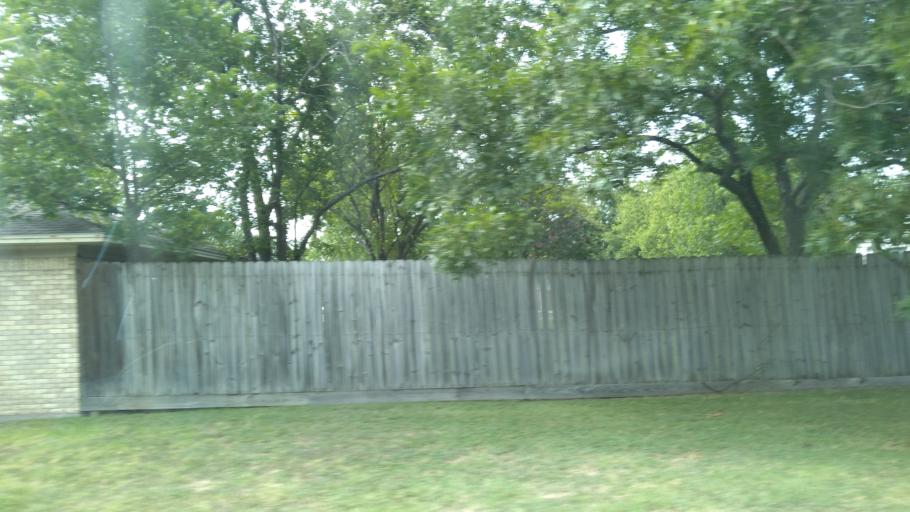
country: US
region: Texas
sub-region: Navarro County
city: Corsicana
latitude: 32.0802
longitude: -96.4876
